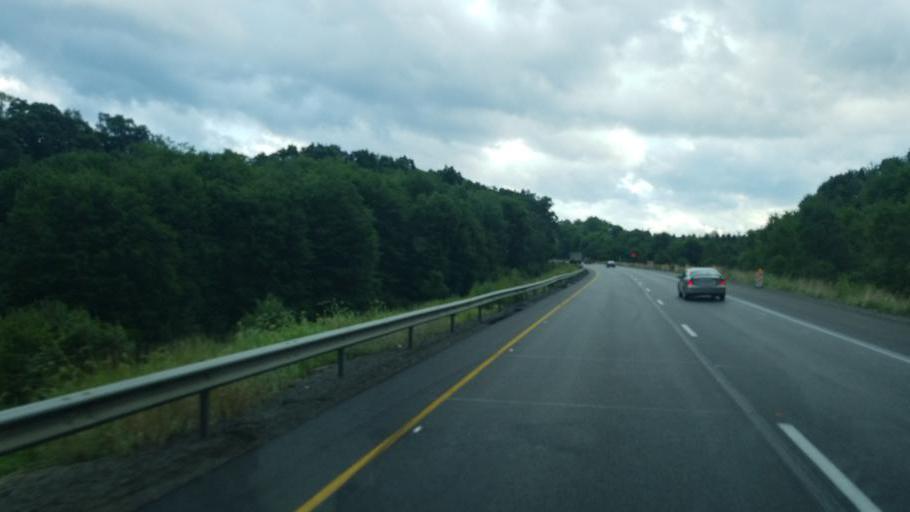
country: US
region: Pennsylvania
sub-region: Butler County
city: Fox Run
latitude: 40.7458
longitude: -80.1078
